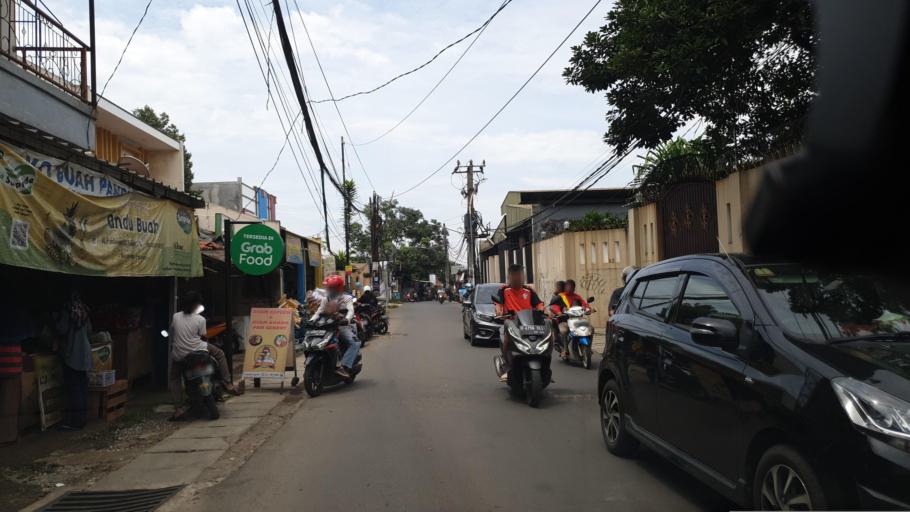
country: ID
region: West Java
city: Pamulang
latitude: -6.3687
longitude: 106.7595
